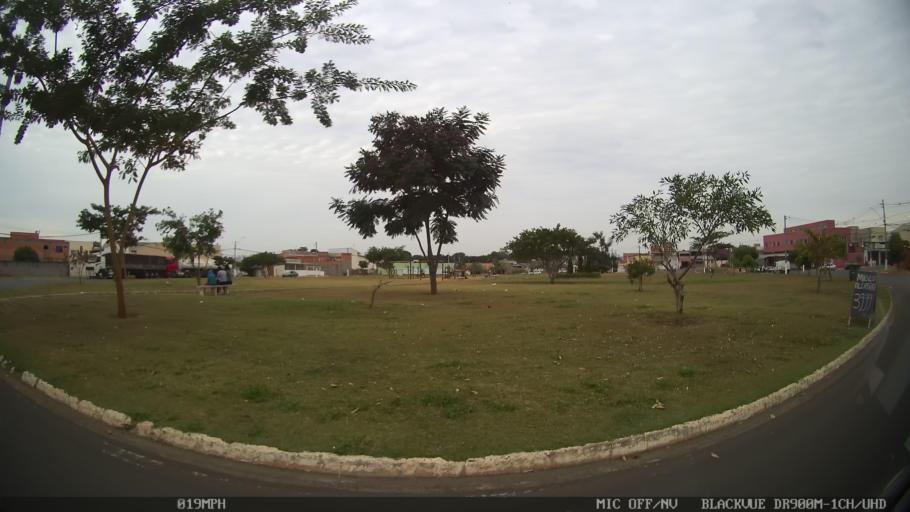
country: BR
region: Sao Paulo
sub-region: Paulinia
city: Paulinia
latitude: -22.7152
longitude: -47.1696
